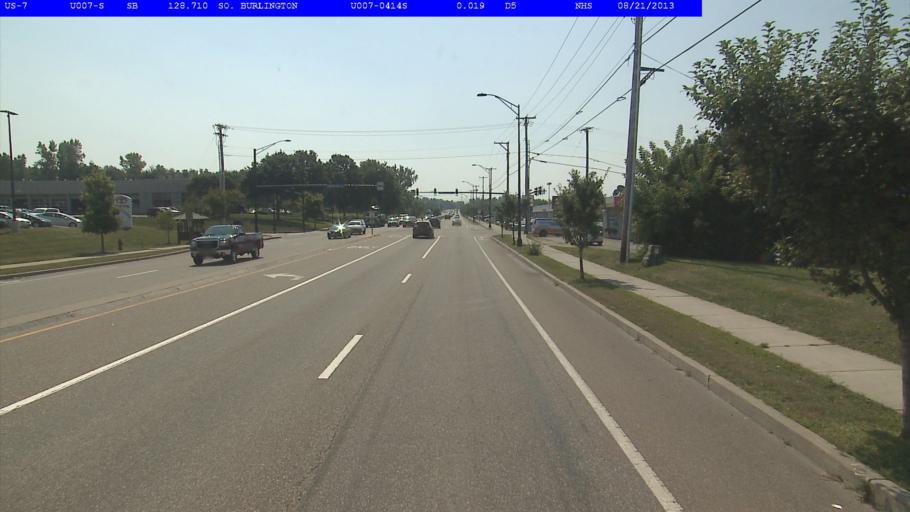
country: US
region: Vermont
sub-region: Chittenden County
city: Burlington
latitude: 44.4291
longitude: -73.2113
